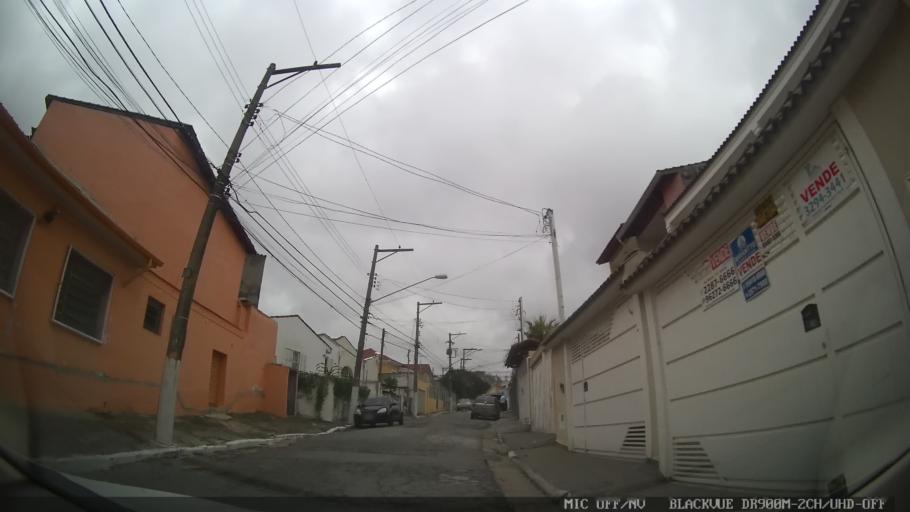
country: BR
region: Sao Paulo
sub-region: Sao Paulo
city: Sao Paulo
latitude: -23.4969
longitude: -46.6062
